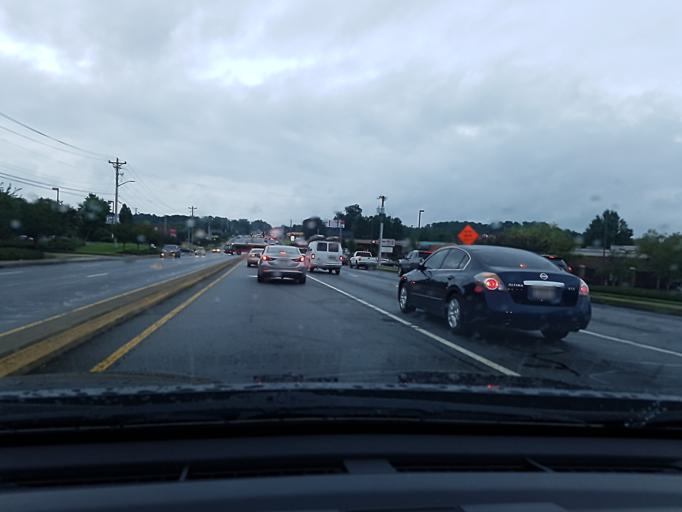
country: US
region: Georgia
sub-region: Gwinnett County
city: Lilburn
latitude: 33.9449
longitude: -84.1250
